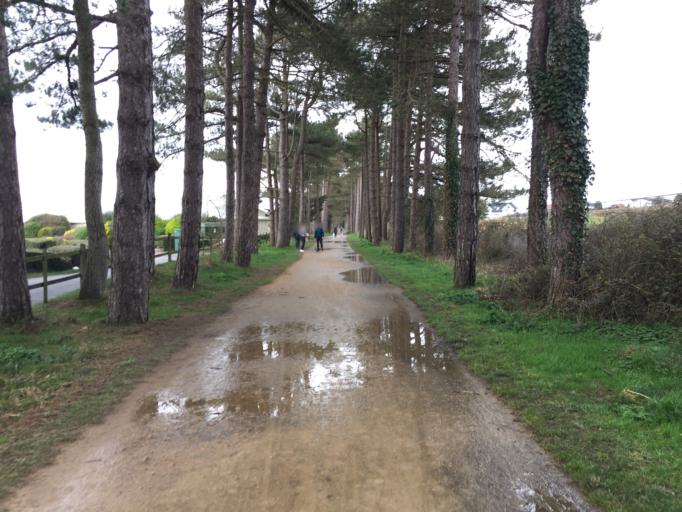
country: JE
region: St Helier
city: Saint Helier
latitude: 49.1897
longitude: -2.2157
